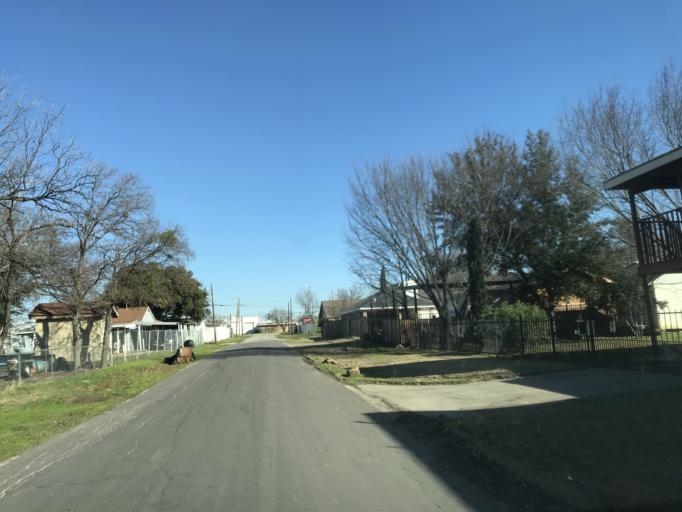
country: US
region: Texas
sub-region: Dallas County
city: Cockrell Hill
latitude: 32.7746
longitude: -96.9067
